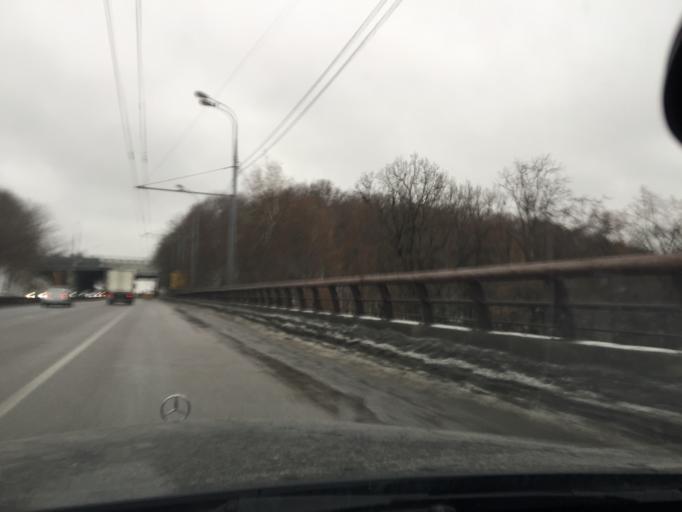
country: RU
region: Moscow
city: Luzhniki
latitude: 55.7081
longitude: 37.5560
